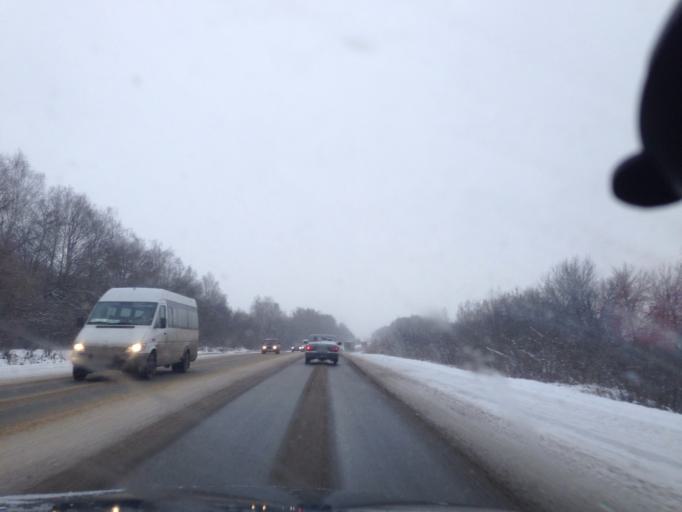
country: RU
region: Tula
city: Bolokhovo
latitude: 54.1006
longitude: 37.7653
